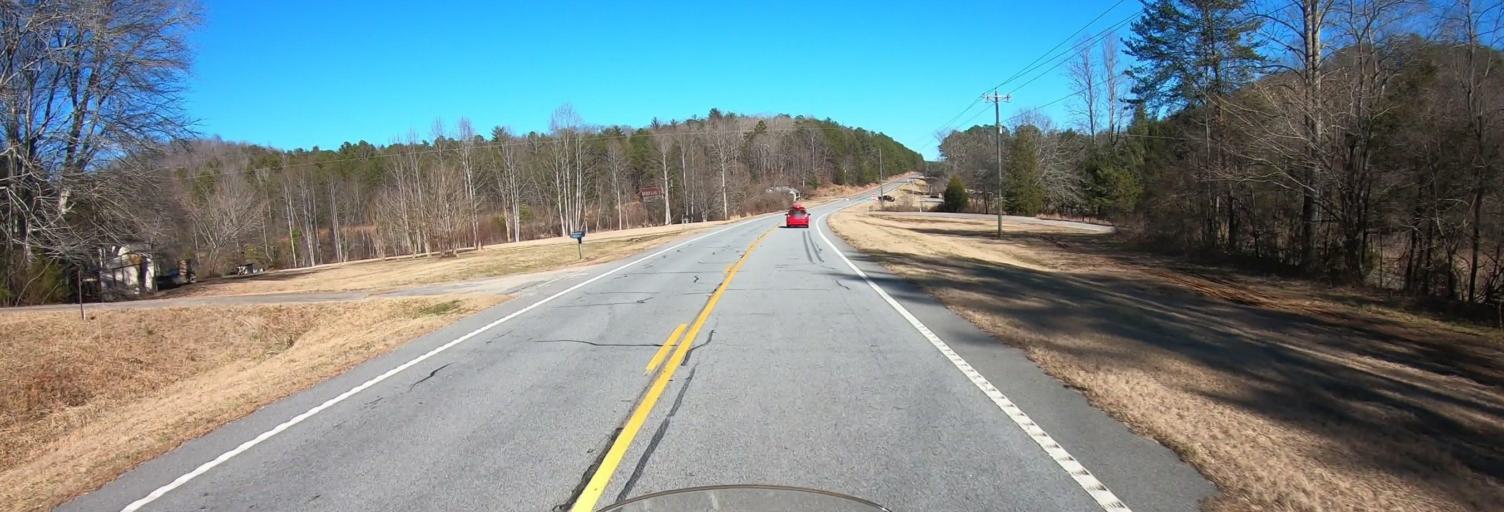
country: US
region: South Carolina
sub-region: Pickens County
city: Pickens
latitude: 34.9753
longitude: -82.8014
